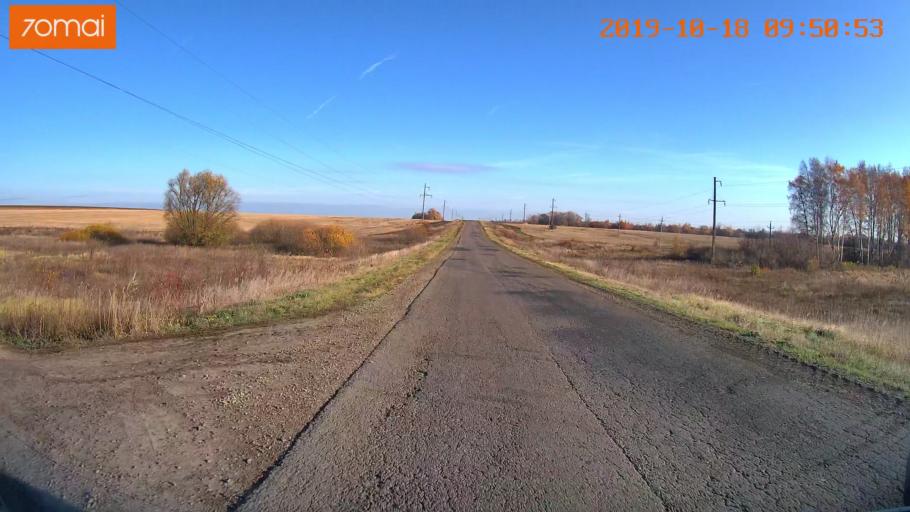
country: RU
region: Tula
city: Kazachka
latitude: 53.3341
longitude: 38.2841
